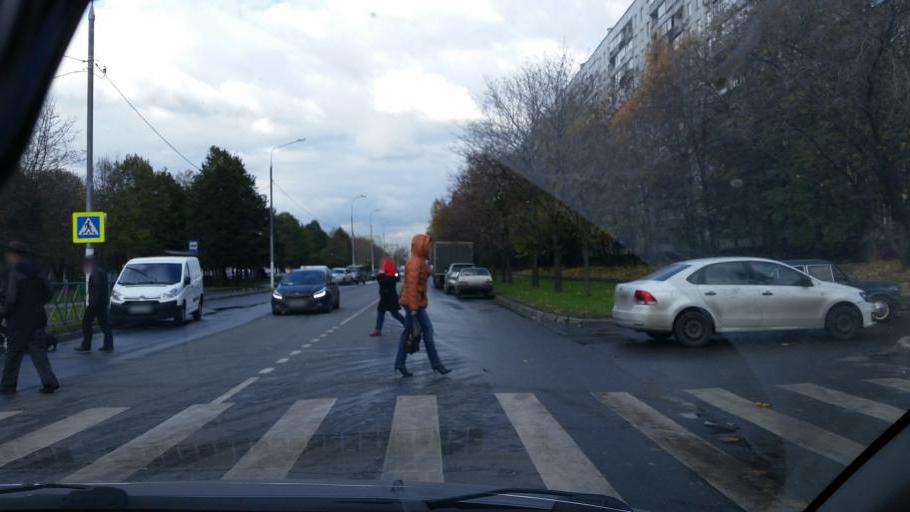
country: RU
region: Moscow
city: Chertanovo Yuzhnoye
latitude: 55.5959
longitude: 37.6058
